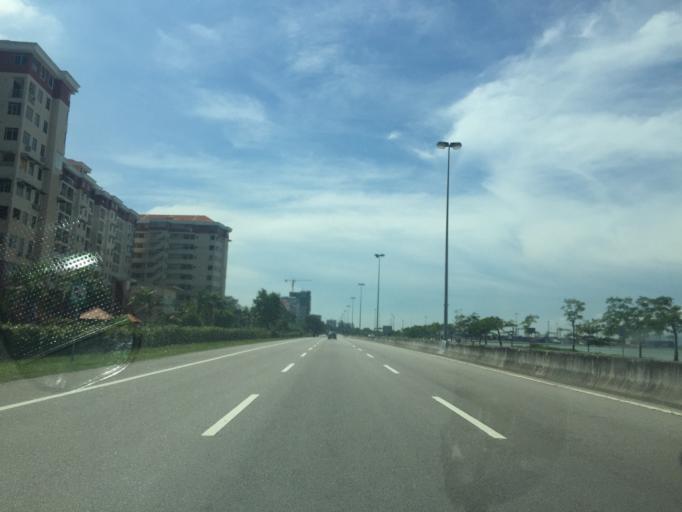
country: MY
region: Penang
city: Butterworth
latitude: 5.4264
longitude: 100.3754
